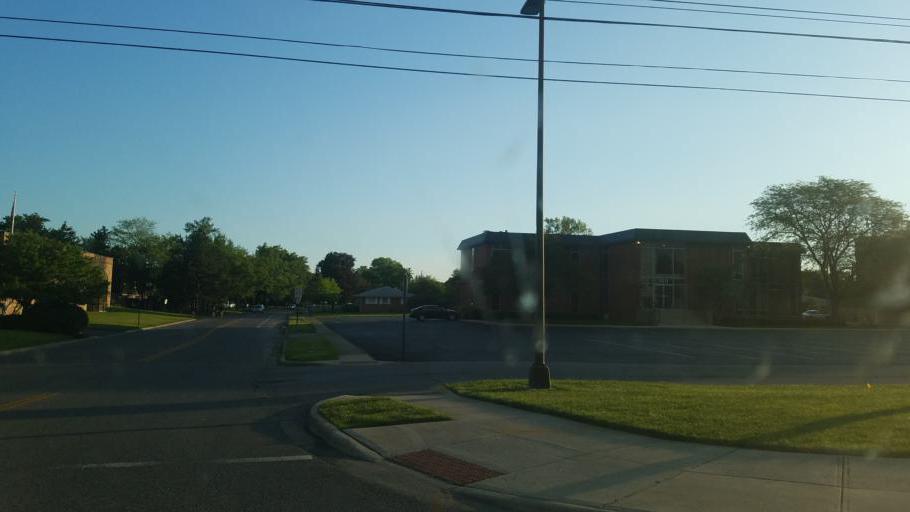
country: US
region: Ohio
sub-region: Franklin County
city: Worthington
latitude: 40.0614
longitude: -82.9905
